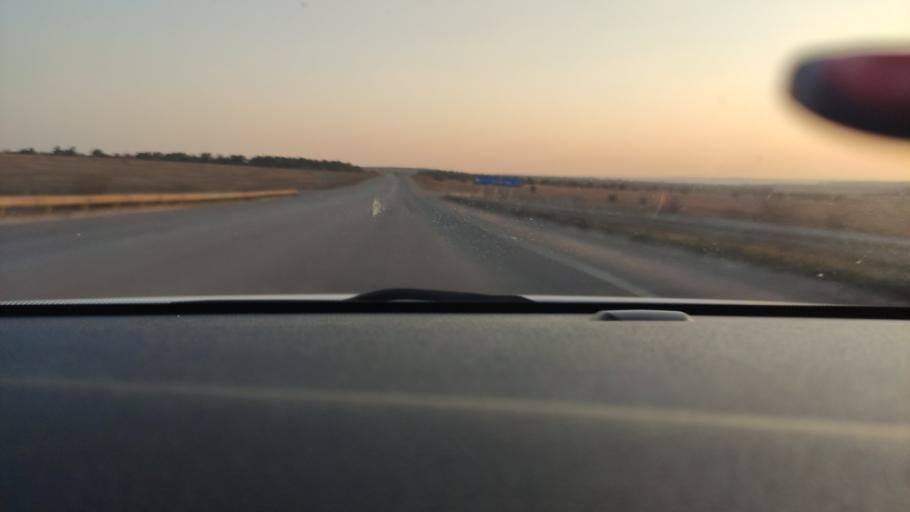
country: RU
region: Voronezj
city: Kolodeznyy
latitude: 51.3876
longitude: 39.2252
